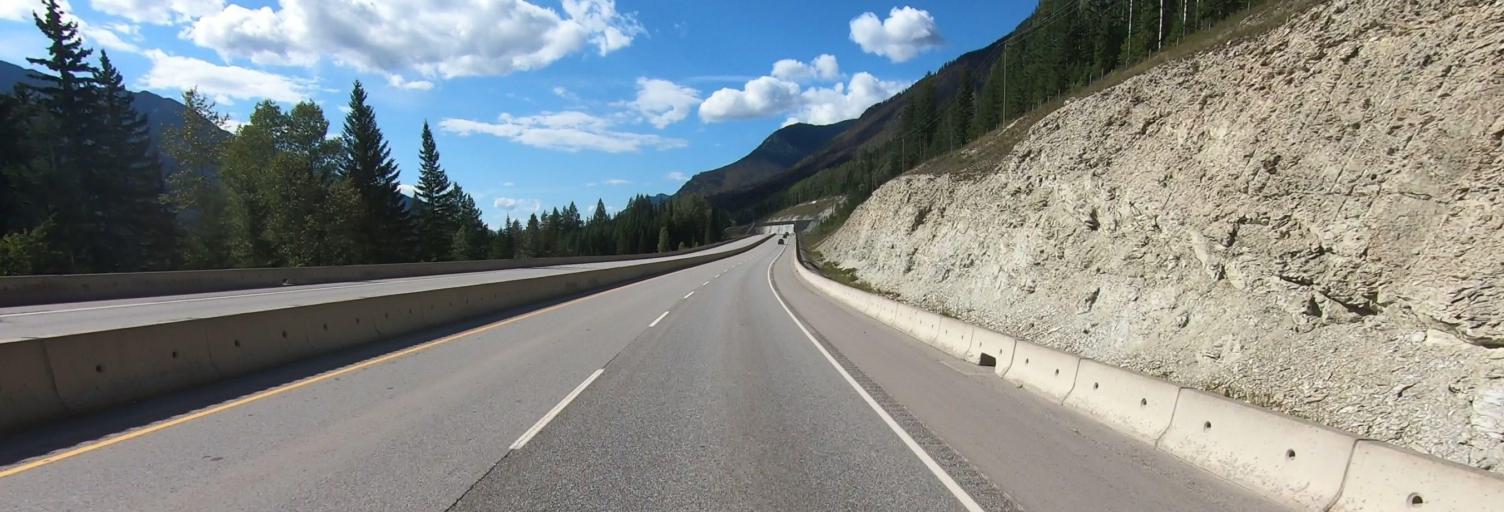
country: CA
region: British Columbia
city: Golden
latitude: 51.2506
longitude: -116.6793
